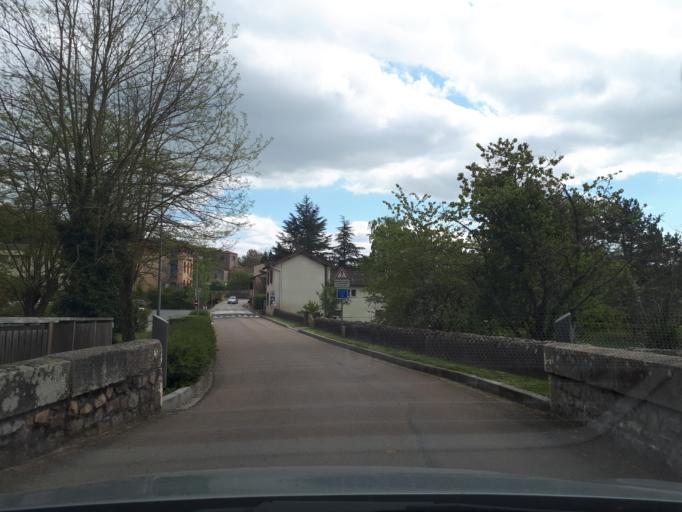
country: FR
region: Rhone-Alpes
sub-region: Departement de la Loire
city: Civens
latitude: 45.7390
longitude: 4.2881
